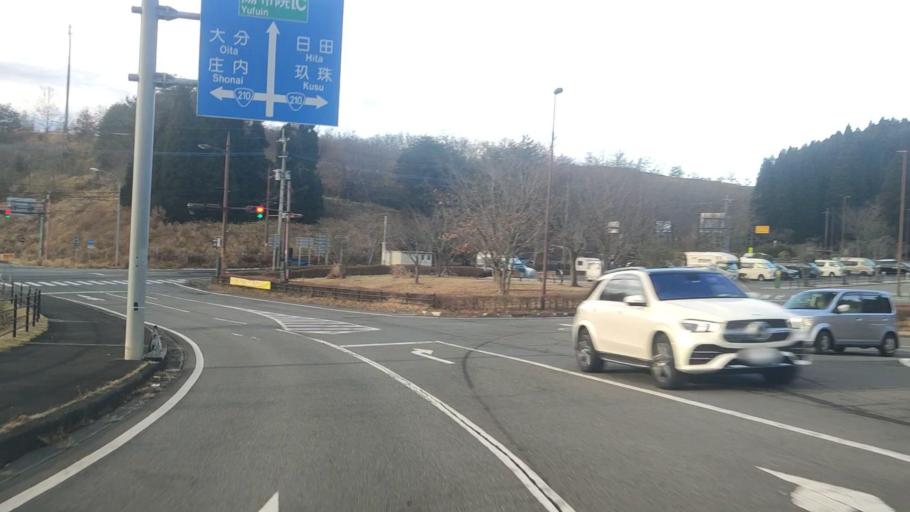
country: JP
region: Oita
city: Beppu
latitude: 33.2607
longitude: 131.3284
